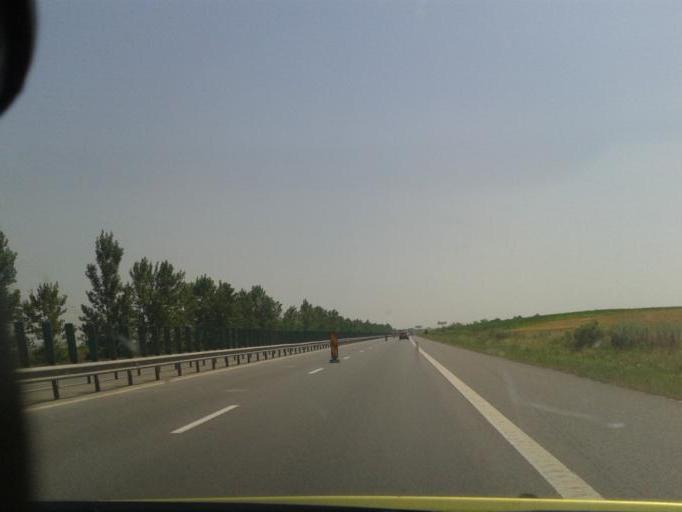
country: RO
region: Calarasi
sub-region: Comuna Tamadau Mare
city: Tamadau Mare
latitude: 44.4447
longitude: 26.5624
